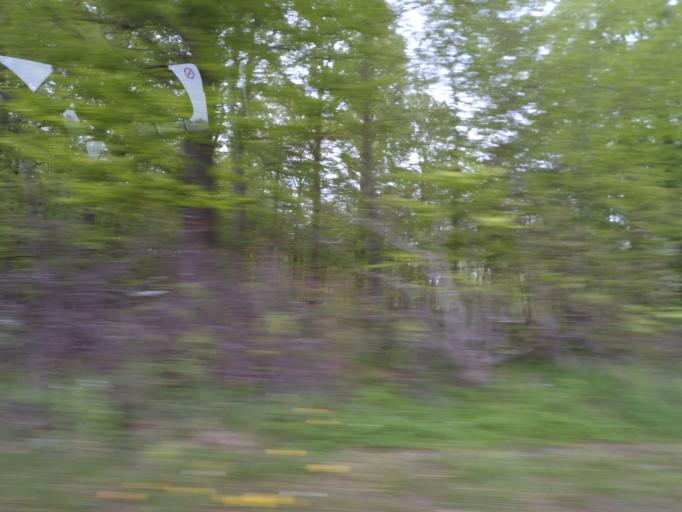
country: DK
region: South Denmark
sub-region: Svendborg Kommune
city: Svendborg
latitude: 55.1672
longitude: 10.6179
